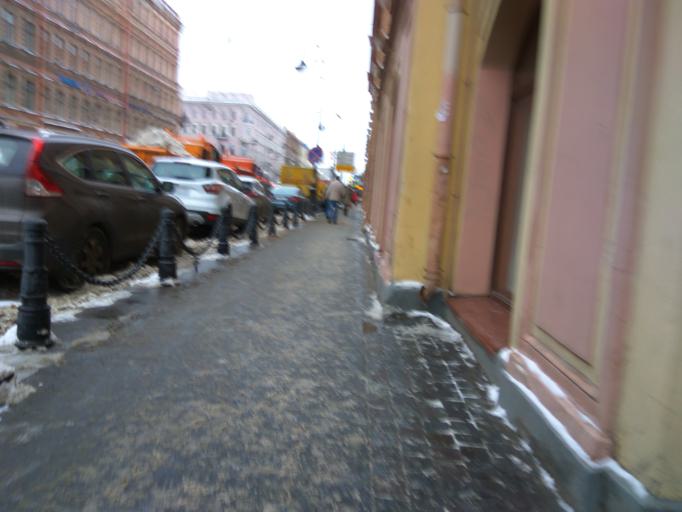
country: RU
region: St.-Petersburg
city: Centralniy
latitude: 59.9317
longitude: 30.3478
